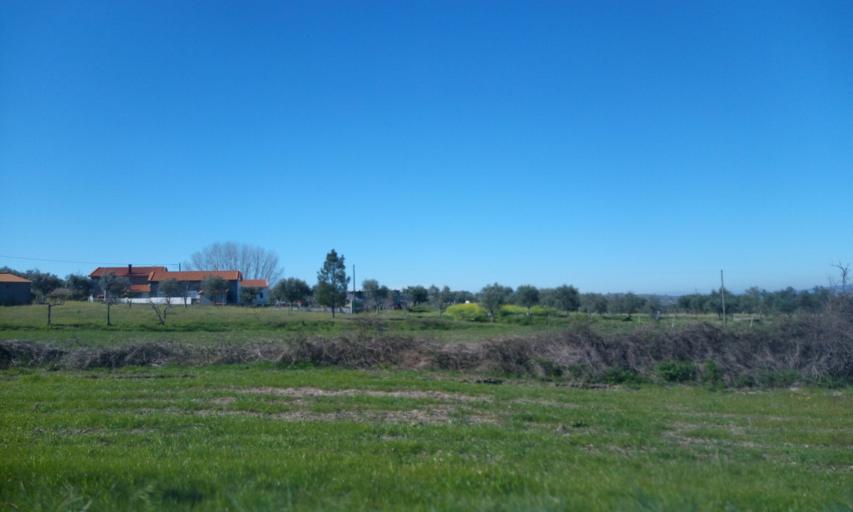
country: PT
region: Guarda
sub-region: Fornos de Algodres
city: Fornos de Algodres
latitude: 40.5277
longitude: -7.5571
